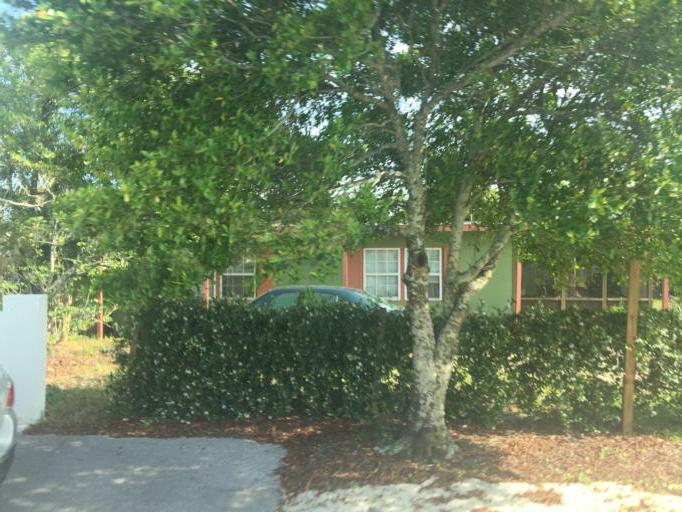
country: US
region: Florida
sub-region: Bay County
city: Laguna Beach
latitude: 30.2543
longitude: -85.9518
